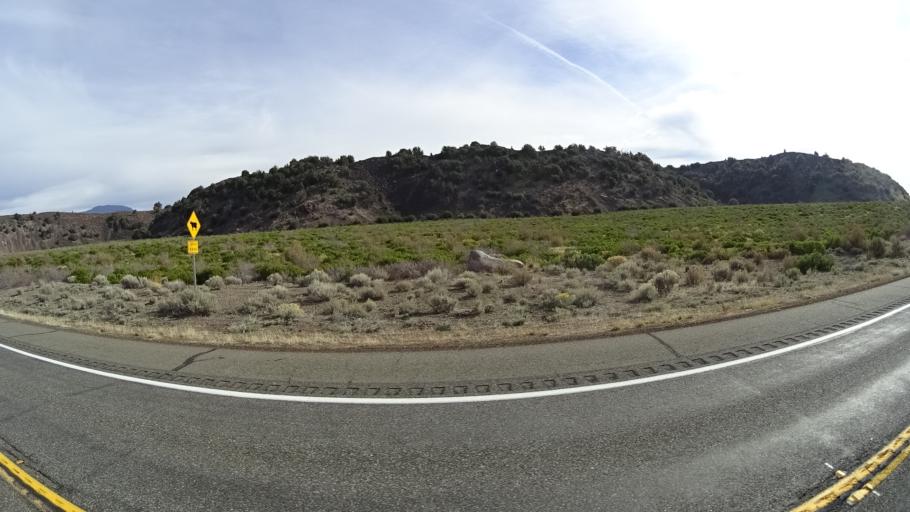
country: US
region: California
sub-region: Siskiyou County
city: Weed
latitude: 41.5147
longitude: -122.3114
